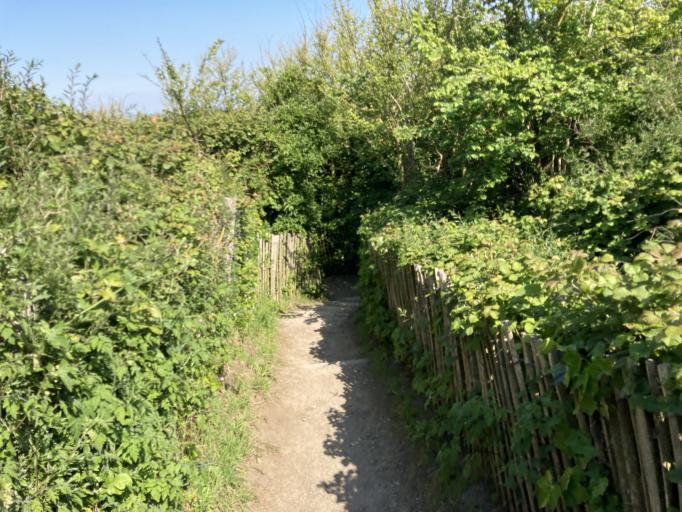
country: FR
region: Nord-Pas-de-Calais
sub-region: Departement du Pas-de-Calais
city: Ambleteuse
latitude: 50.8703
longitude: 1.5878
